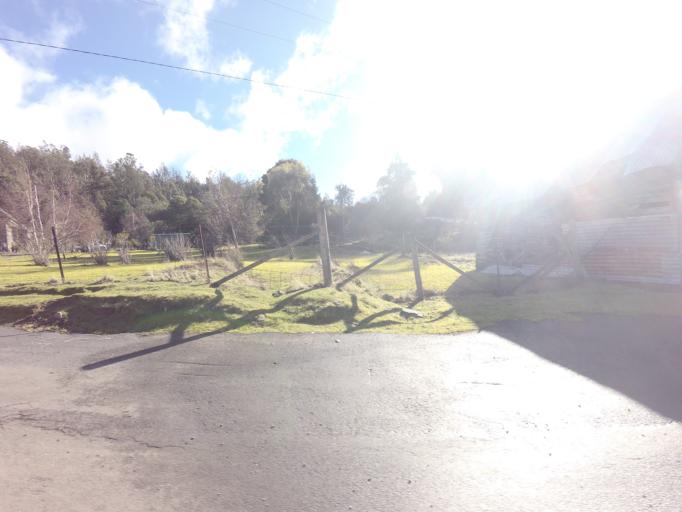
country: AU
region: Tasmania
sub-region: Glenorchy
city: Berriedale
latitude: -42.8506
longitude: 147.1684
